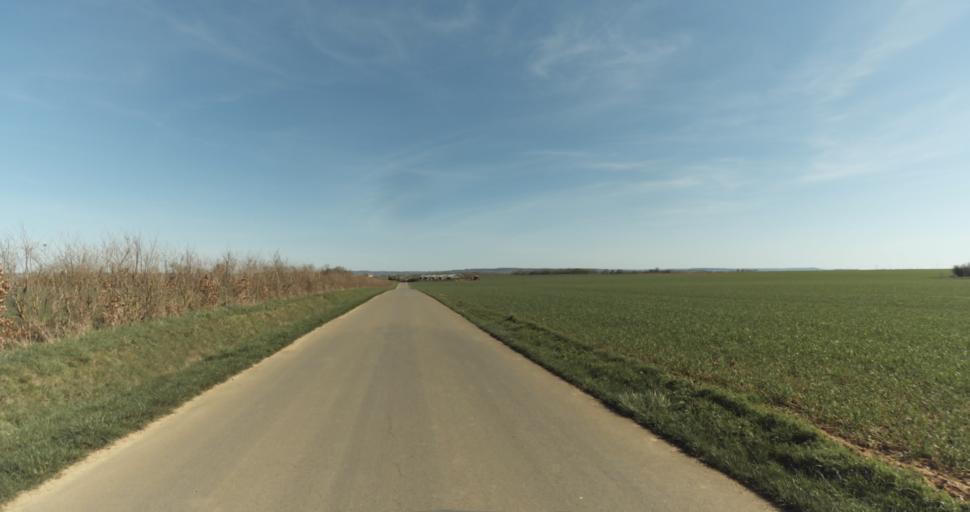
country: FR
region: Lower Normandy
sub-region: Departement du Calvados
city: Canon
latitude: 49.0489
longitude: -0.0605
